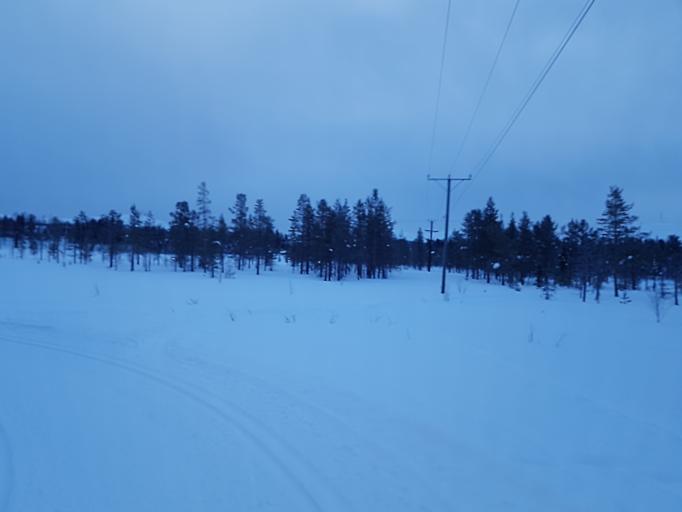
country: FI
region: Lapland
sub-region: Tunturi-Lappi
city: Kolari
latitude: 67.6148
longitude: 24.1405
